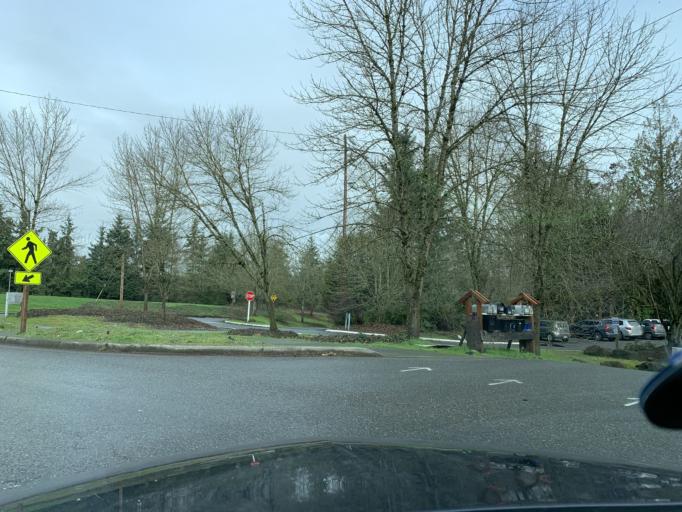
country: US
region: Washington
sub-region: King County
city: Mercer Island
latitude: 47.5765
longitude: -122.2060
